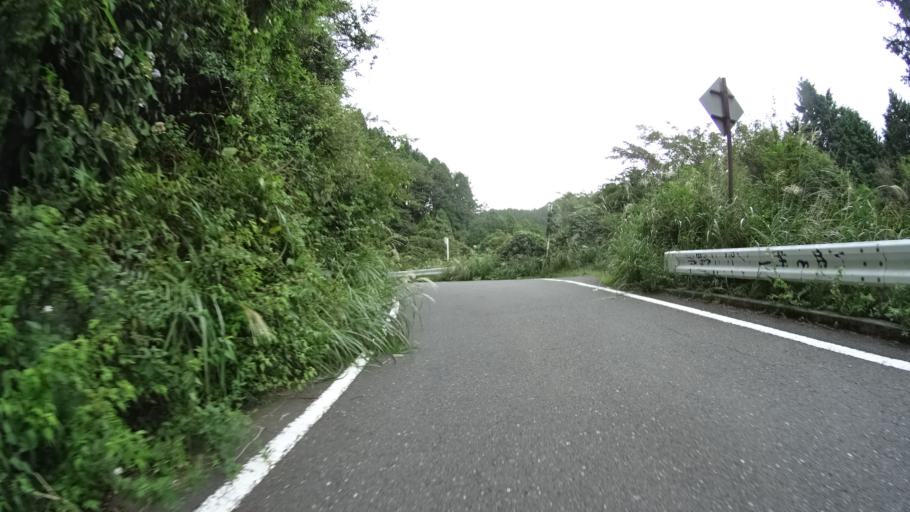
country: JP
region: Kanagawa
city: Hadano
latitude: 35.4260
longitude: 139.2221
